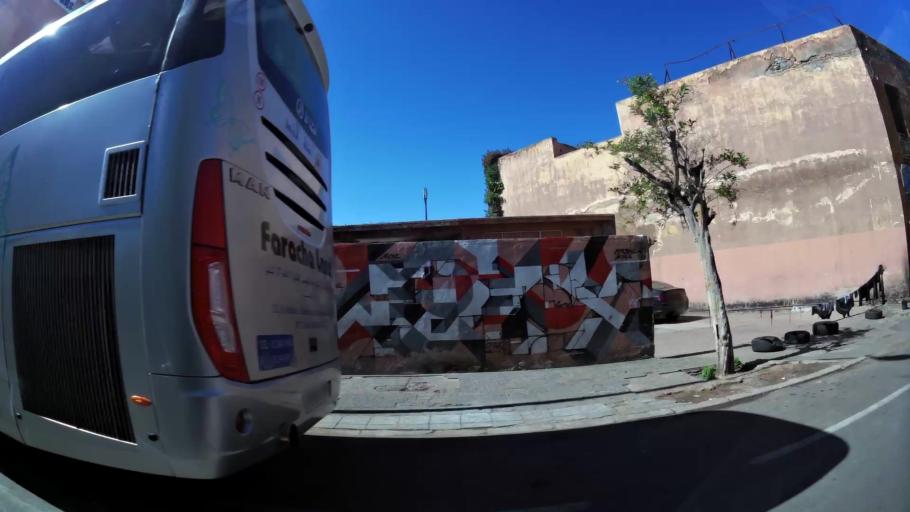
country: MA
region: Marrakech-Tensift-Al Haouz
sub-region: Marrakech
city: Marrakesh
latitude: 31.6337
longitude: -8.0128
